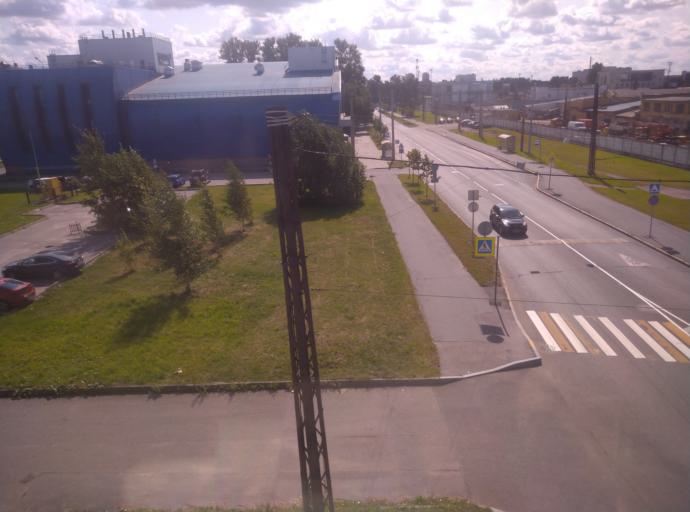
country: RU
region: St.-Petersburg
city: Centralniy
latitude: 59.9125
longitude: 30.3998
